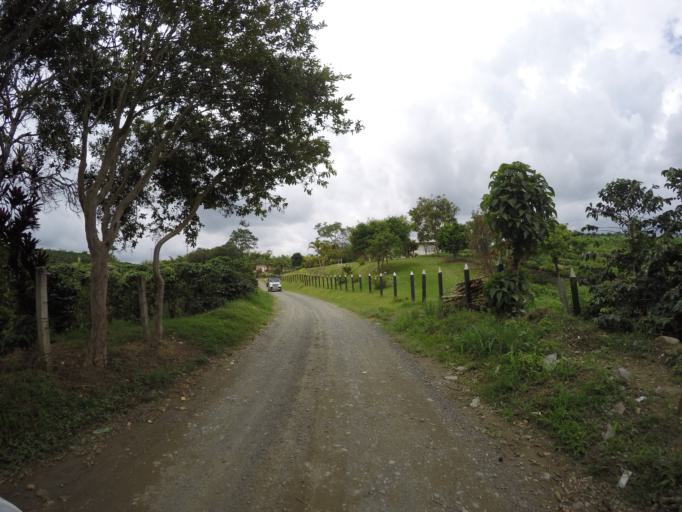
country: CO
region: Quindio
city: Circasia
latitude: 4.6193
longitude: -75.6946
